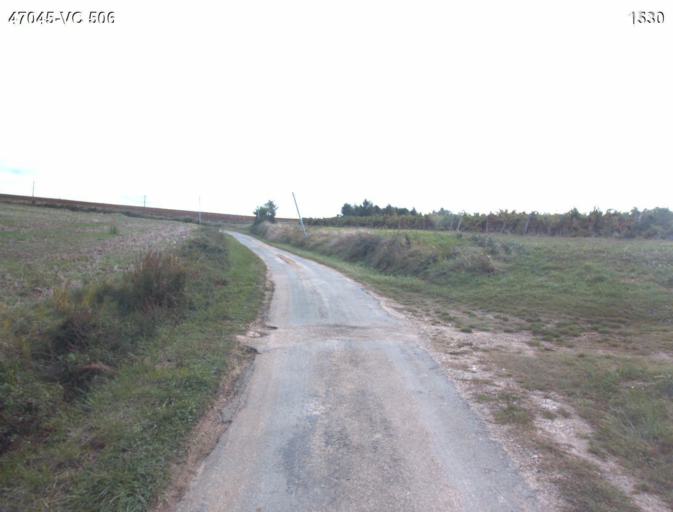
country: FR
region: Aquitaine
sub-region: Departement du Lot-et-Garonne
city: Nerac
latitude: 44.1228
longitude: 0.4039
